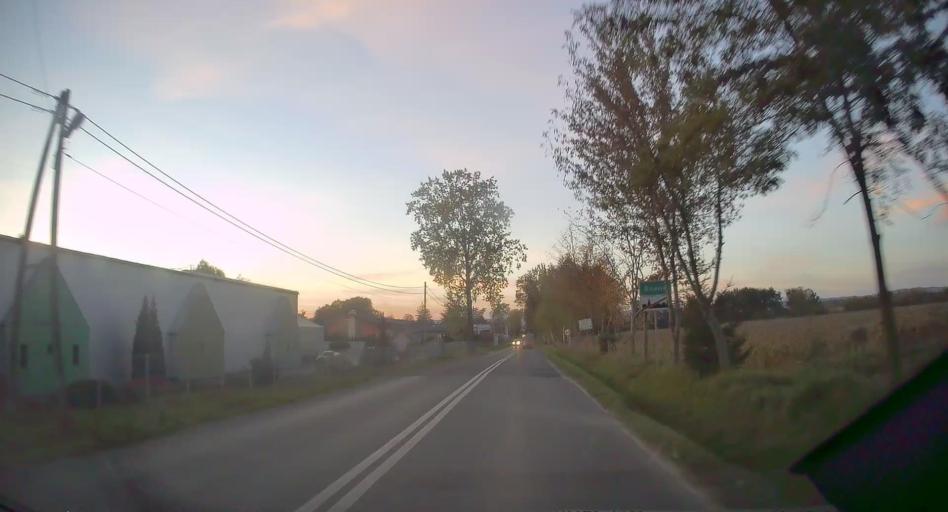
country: PL
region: Lesser Poland Voivodeship
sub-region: Powiat krakowski
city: Rzaska
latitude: 50.1142
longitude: 19.8333
